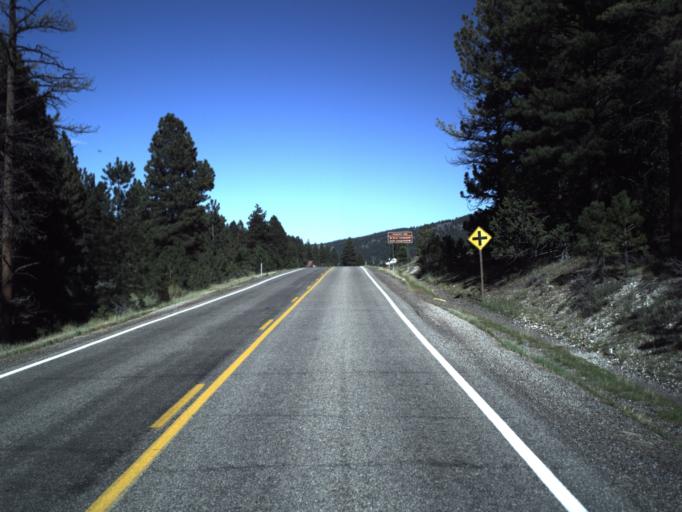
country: US
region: Utah
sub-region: Iron County
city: Parowan
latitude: 37.7004
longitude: -112.6579
